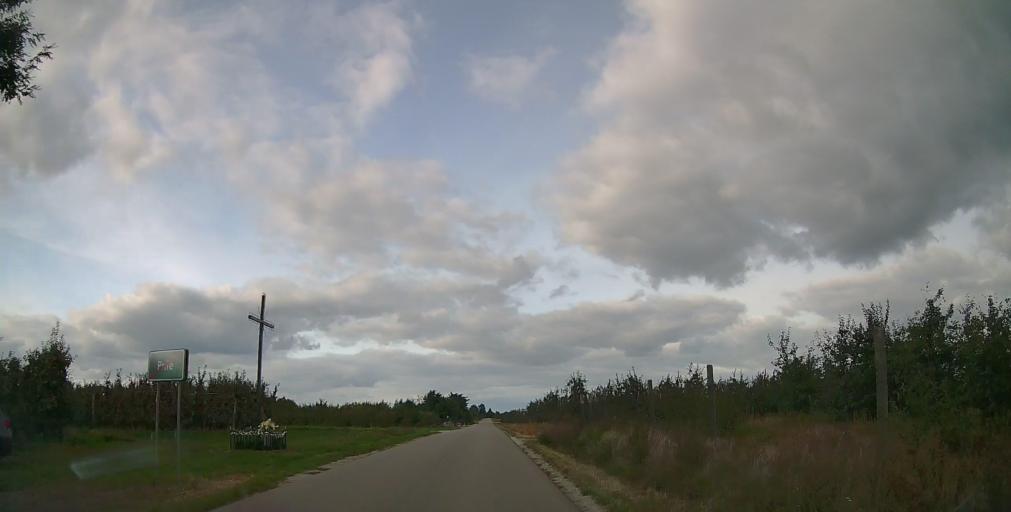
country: PL
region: Masovian Voivodeship
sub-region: Powiat bialobrzeski
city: Promna
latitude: 51.7175
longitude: 20.9584
